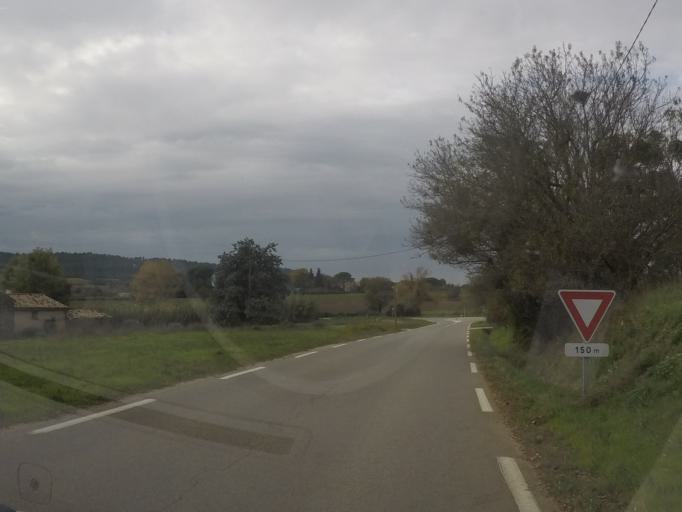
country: FR
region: Provence-Alpes-Cote d'Azur
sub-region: Departement du Vaucluse
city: Ansouis
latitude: 43.7436
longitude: 5.4420
